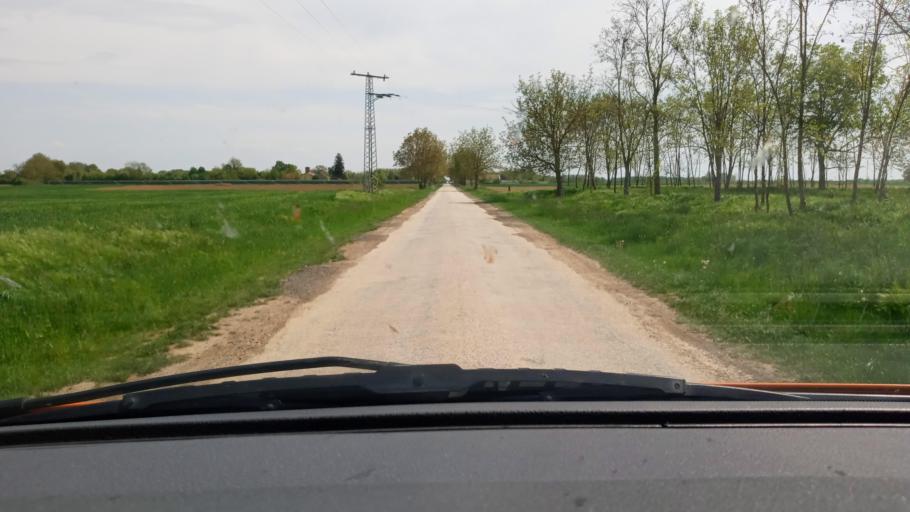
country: HU
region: Baranya
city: Beremend
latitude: 45.8093
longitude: 18.5157
